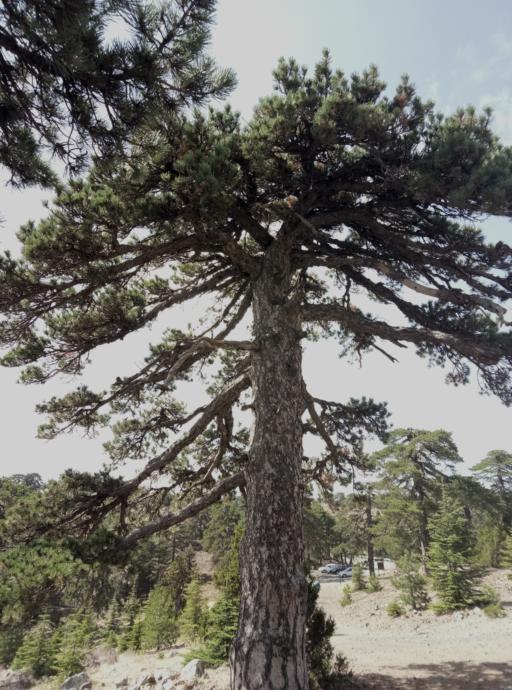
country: CY
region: Lefkosia
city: Kakopetria
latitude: 34.9333
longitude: 32.8734
